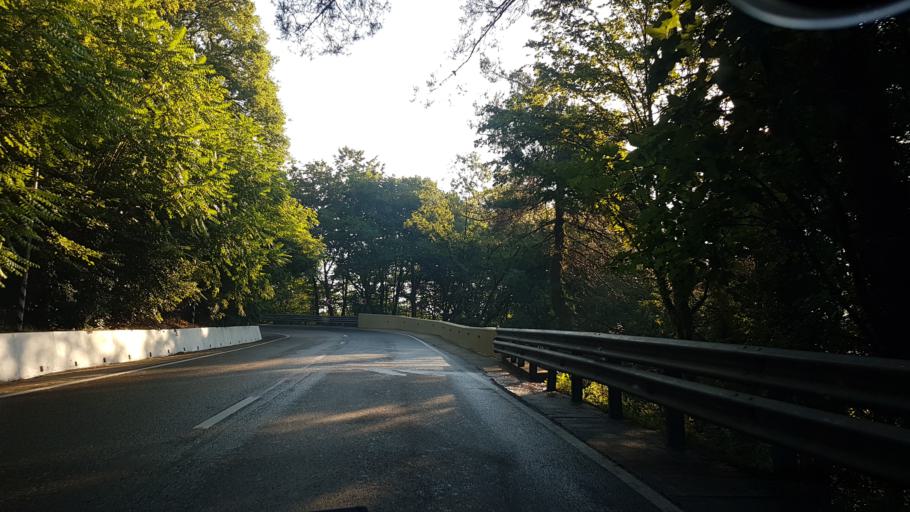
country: RU
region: Krasnodarskiy
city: Dagomys
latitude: 43.6451
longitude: 39.6960
